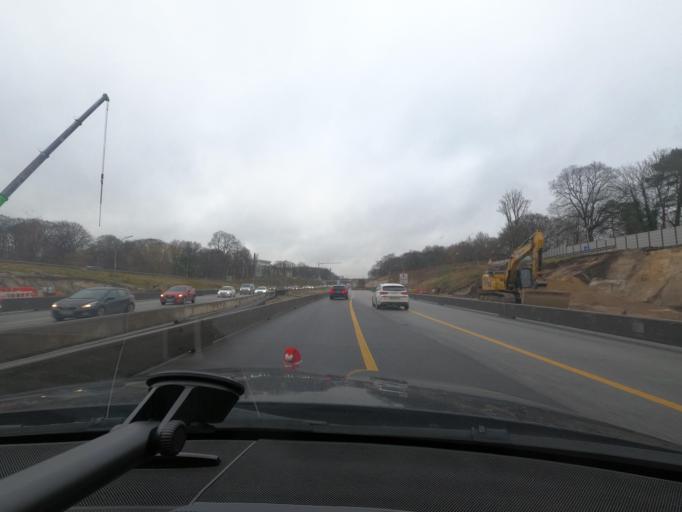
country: DE
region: Hamburg
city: Altona
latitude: 53.5644
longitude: 9.8983
